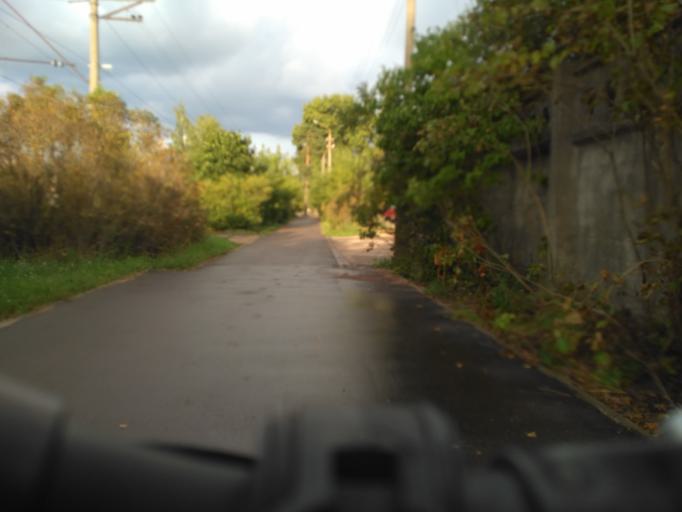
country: RU
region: Moskovskaya
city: Dubna
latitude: 56.7439
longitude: 37.1867
